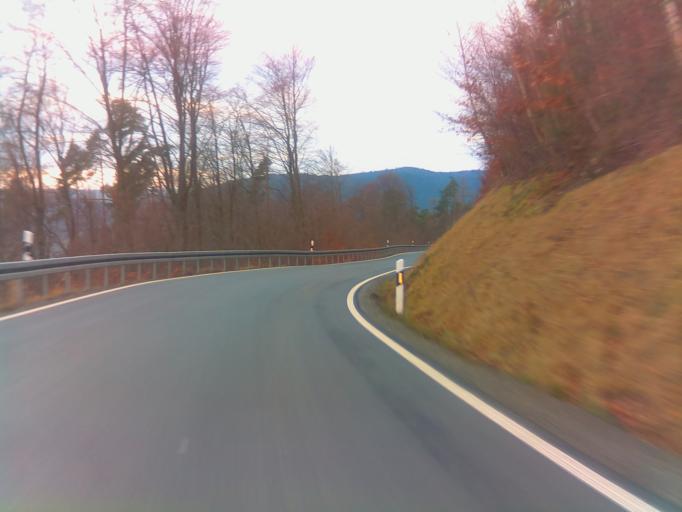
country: DE
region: Bavaria
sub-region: Regierungsbezirk Unterfranken
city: Miltenberg
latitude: 49.6917
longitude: 9.2865
